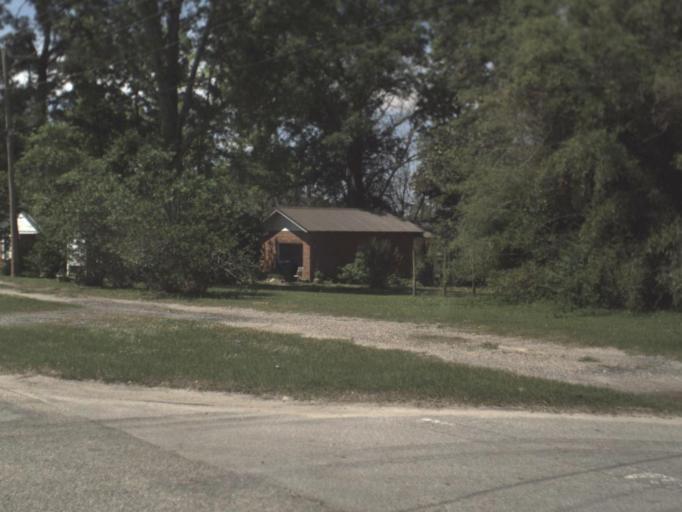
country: US
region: Florida
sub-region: Jackson County
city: Marianna
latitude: 30.7554
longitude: -85.2296
